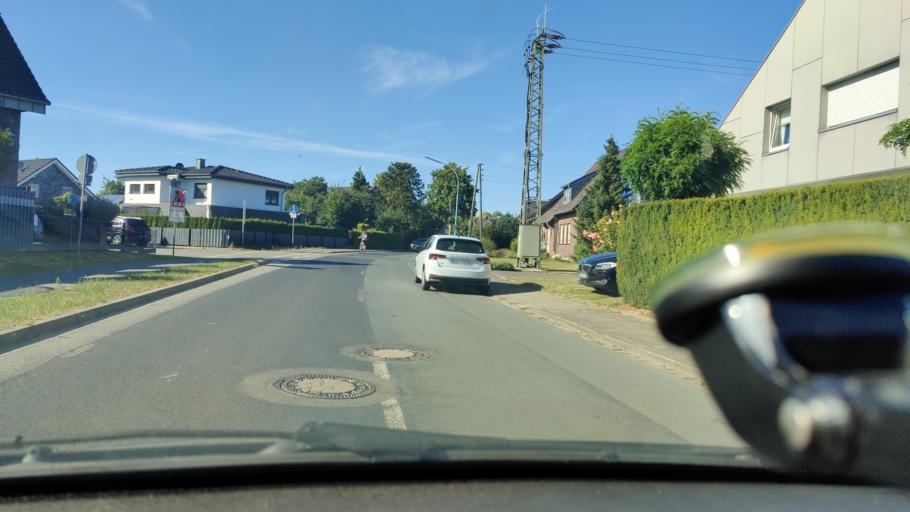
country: DE
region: North Rhine-Westphalia
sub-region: Regierungsbezirk Dusseldorf
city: Kleve
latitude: 51.7681
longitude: 6.2086
